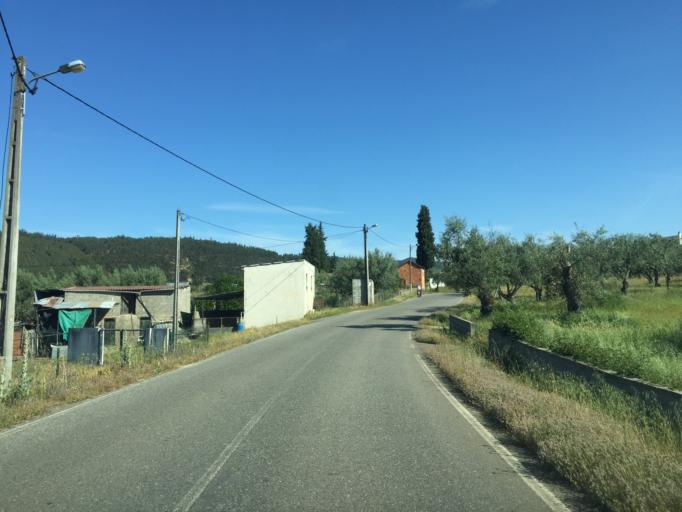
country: PT
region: Coimbra
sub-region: Pampilhosa da Serra
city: Pampilhosa da Serra
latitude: 40.0636
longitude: -7.8007
